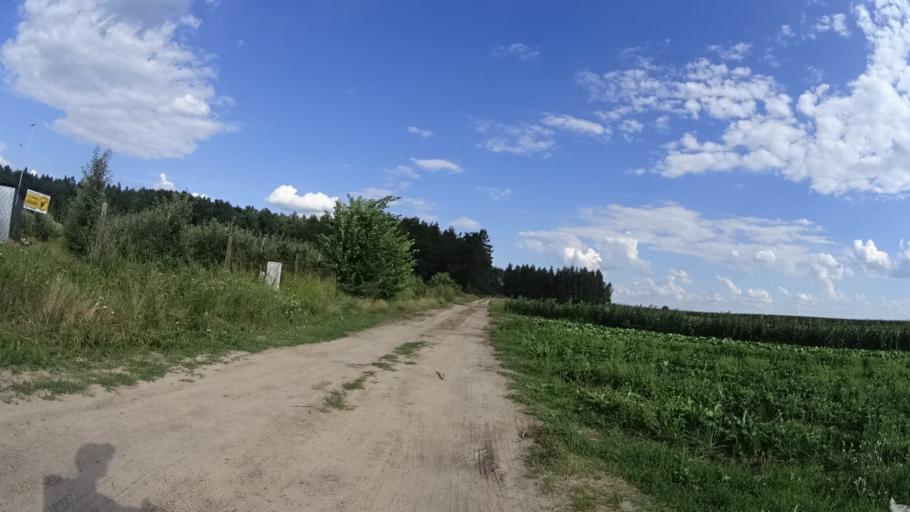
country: PL
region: Masovian Voivodeship
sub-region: Powiat grojecki
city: Mogielnica
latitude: 51.6766
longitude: 20.7791
